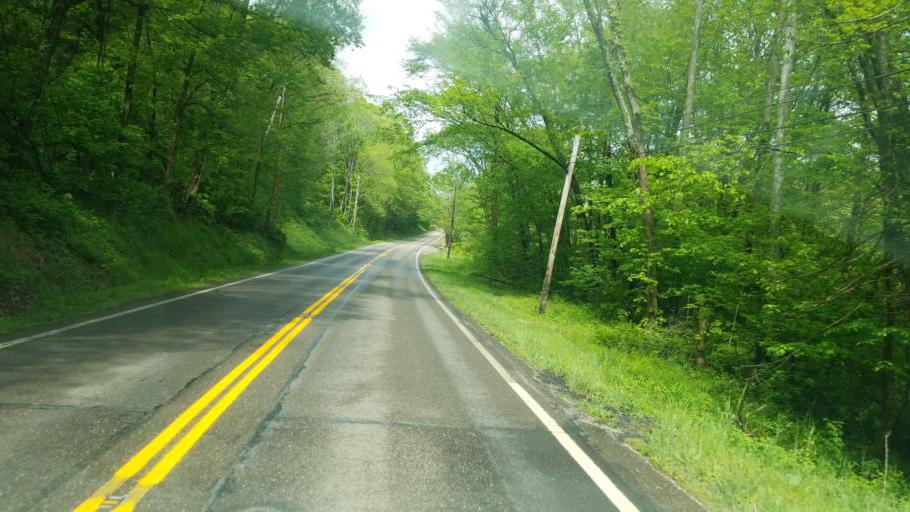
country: US
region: Ohio
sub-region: Tuscarawas County
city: Dover
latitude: 40.5537
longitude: -81.4203
